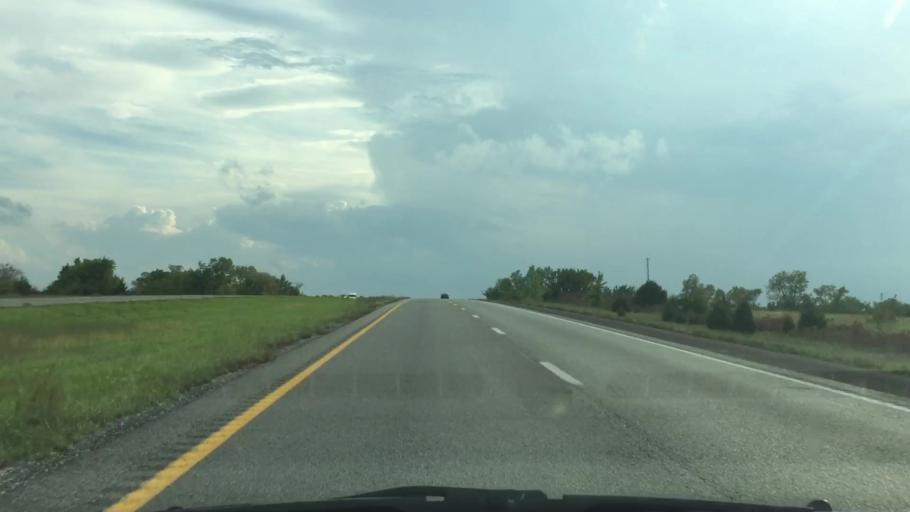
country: US
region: Missouri
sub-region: Daviess County
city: Gallatin
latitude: 39.9224
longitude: -94.1395
